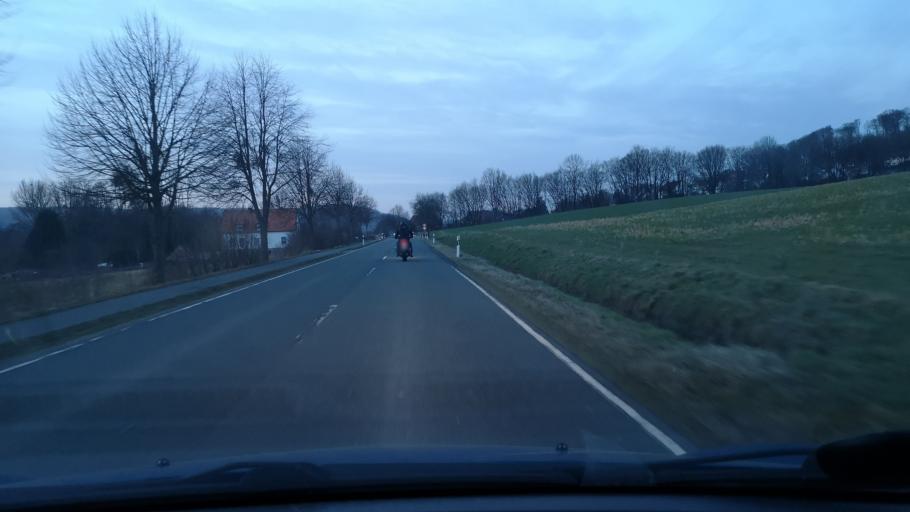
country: DE
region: Lower Saxony
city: Salzhemmendorf
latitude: 52.0581
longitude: 9.5925
